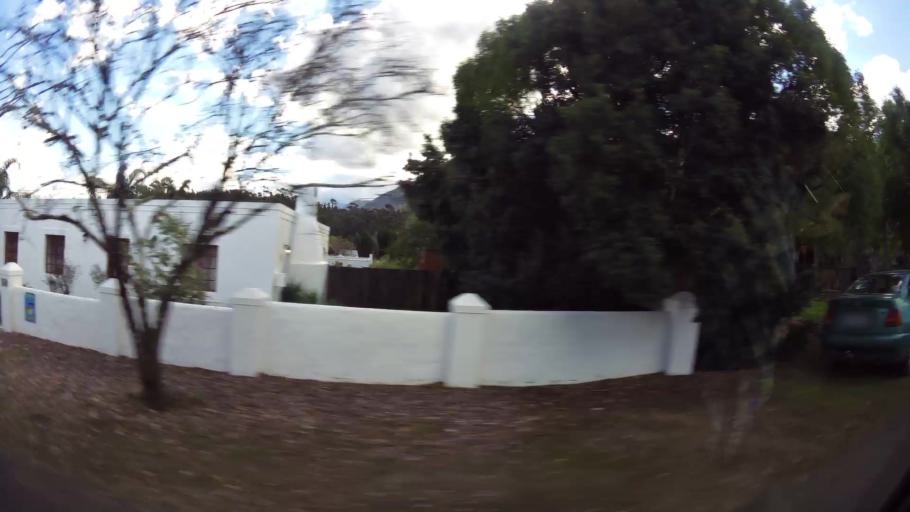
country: ZA
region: Western Cape
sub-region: Overberg District Municipality
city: Swellendam
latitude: -34.0122
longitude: 20.4576
